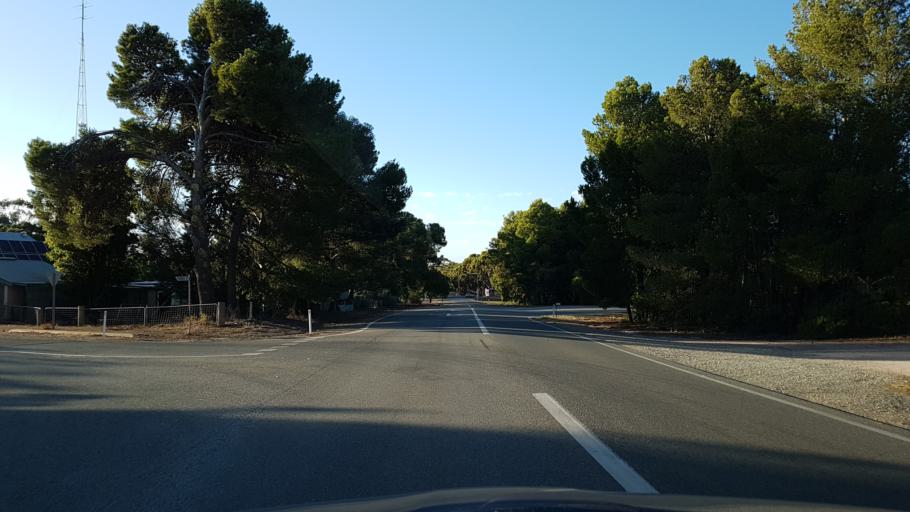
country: AU
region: South Australia
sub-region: Port Pirie City and Dists
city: Crystal Brook
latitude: -33.2704
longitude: 138.3520
